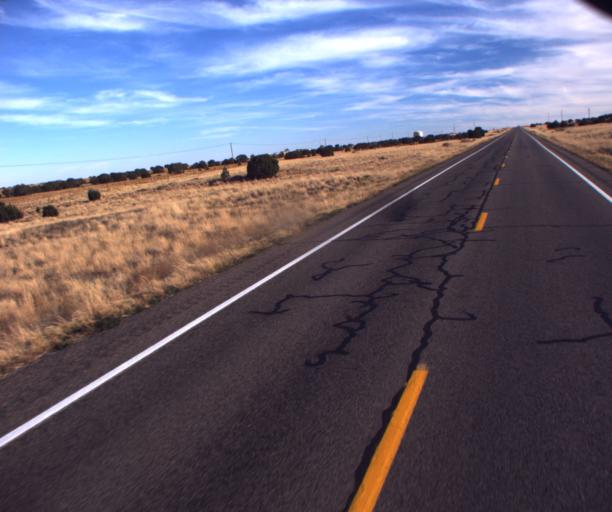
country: US
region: New Mexico
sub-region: San Juan County
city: Shiprock
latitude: 36.9020
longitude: -109.0679
